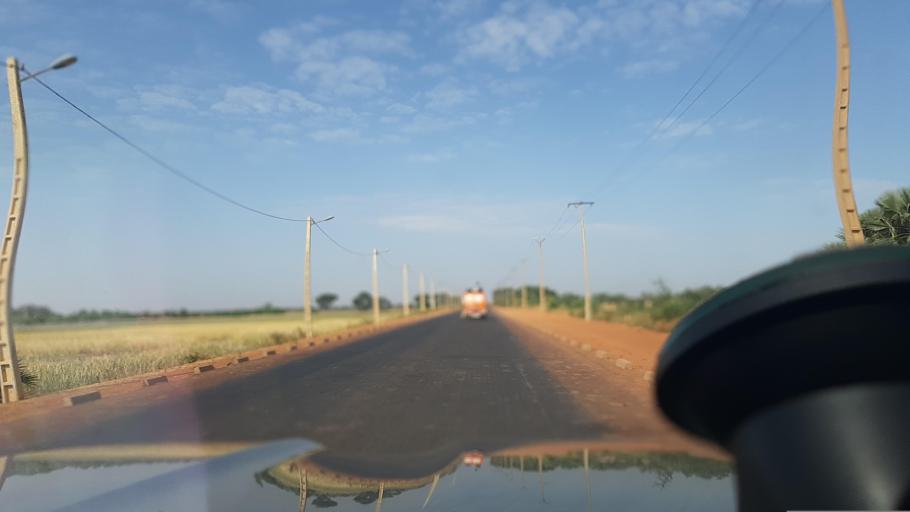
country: ML
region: Segou
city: Markala
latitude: 13.6842
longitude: -6.0934
